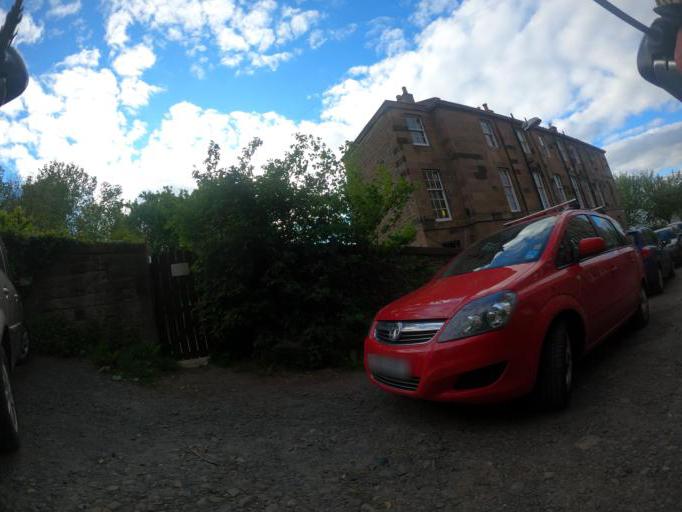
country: GB
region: Scotland
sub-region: Edinburgh
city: Edinburgh
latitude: 55.9790
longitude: -3.2040
